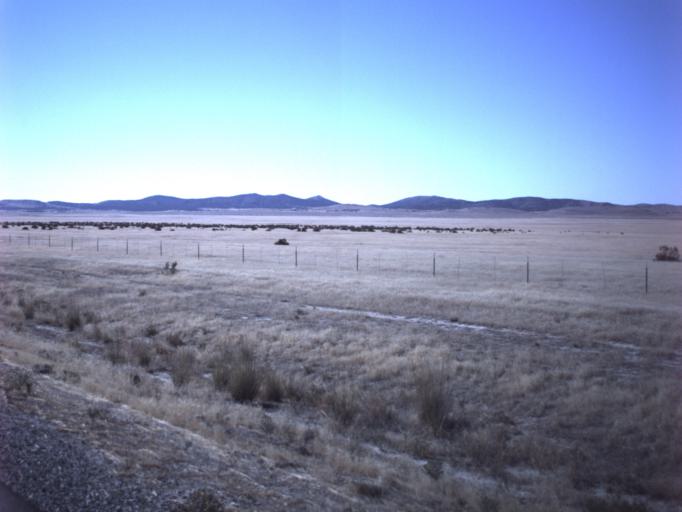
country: US
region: Utah
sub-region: Tooele County
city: Grantsville
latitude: 40.3196
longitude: -112.7438
